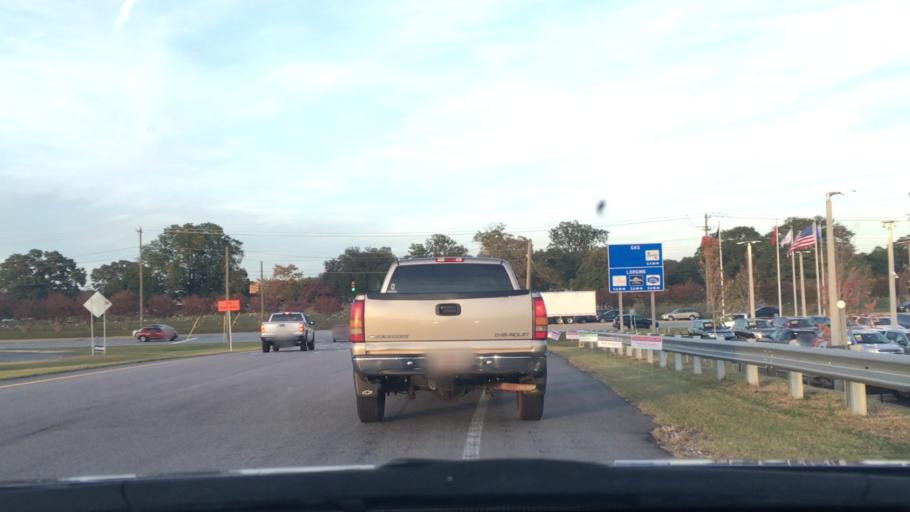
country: US
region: South Carolina
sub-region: Richland County
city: Forest Acres
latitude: 33.9718
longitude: -80.9535
